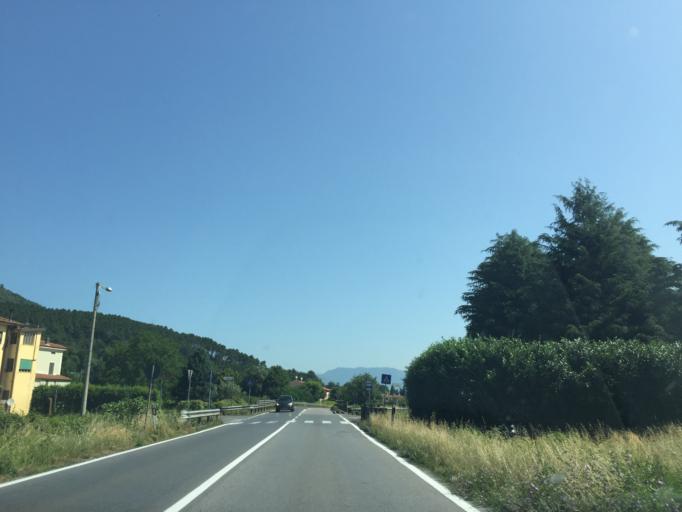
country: IT
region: Tuscany
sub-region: Province of Pisa
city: Asciano
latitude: 43.7908
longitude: 10.4752
